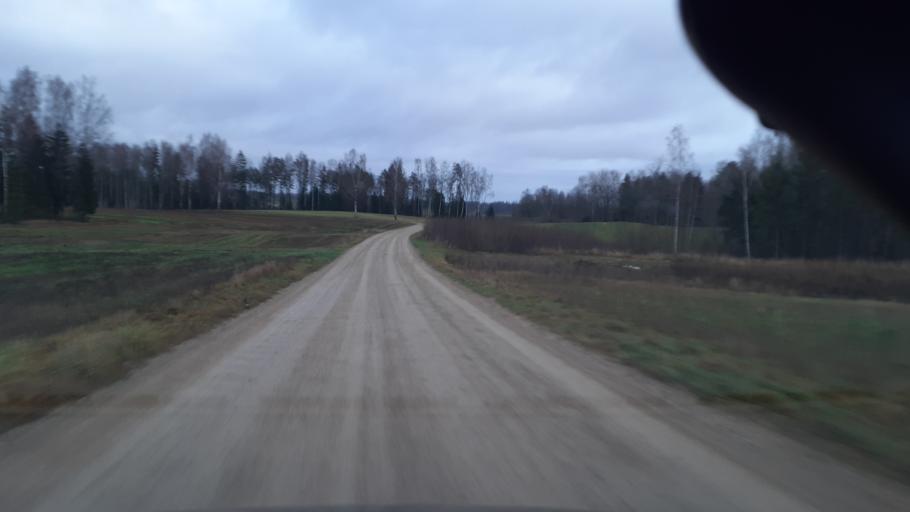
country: LV
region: Alsunga
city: Alsunga
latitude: 56.8935
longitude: 21.7032
